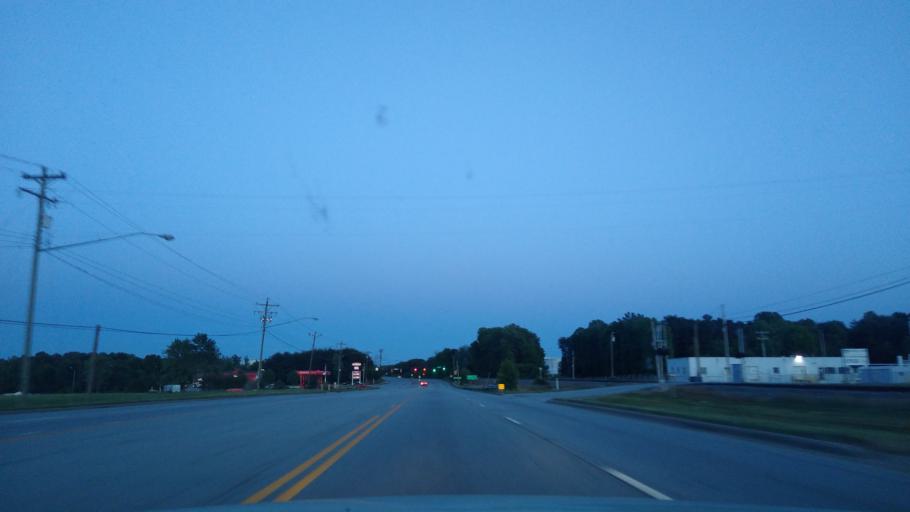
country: US
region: North Carolina
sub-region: Guilford County
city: Jamestown
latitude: 36.0823
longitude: -79.9337
